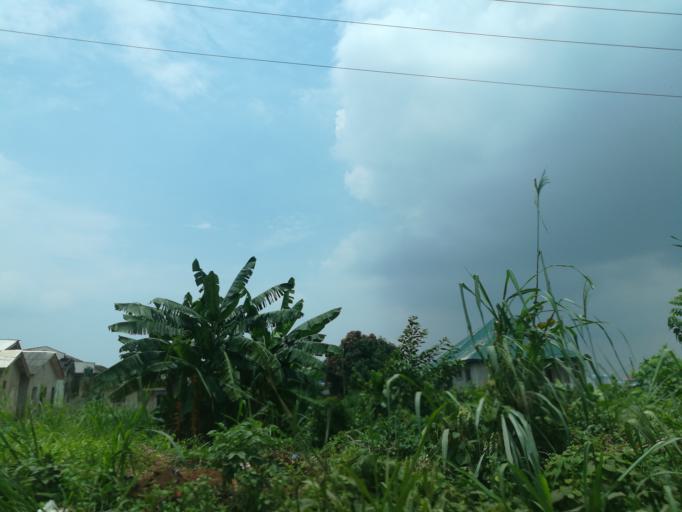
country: NG
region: Lagos
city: Ikorodu
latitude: 6.6228
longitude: 3.5556
